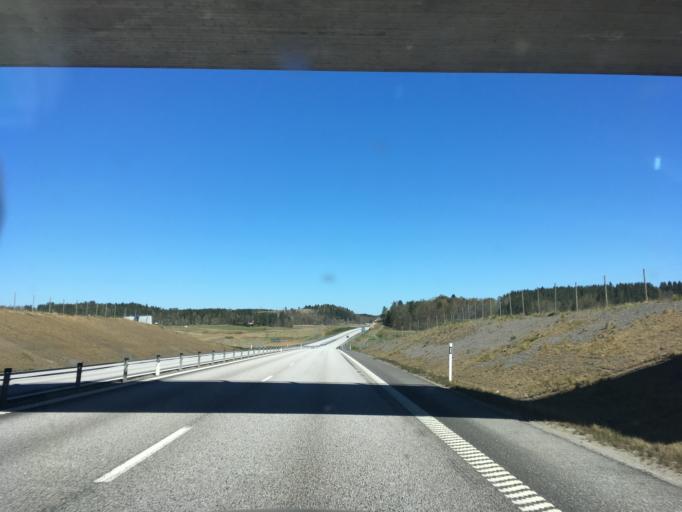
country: SE
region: Vaestra Goetaland
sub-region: Lilla Edets Kommun
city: Lodose
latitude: 58.0272
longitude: 12.1767
